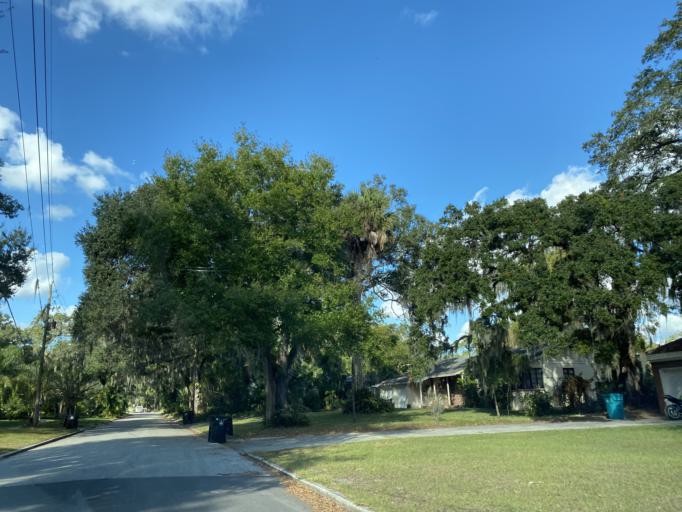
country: US
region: Florida
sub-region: Orange County
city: Orlando
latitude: 28.5499
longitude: -81.4005
